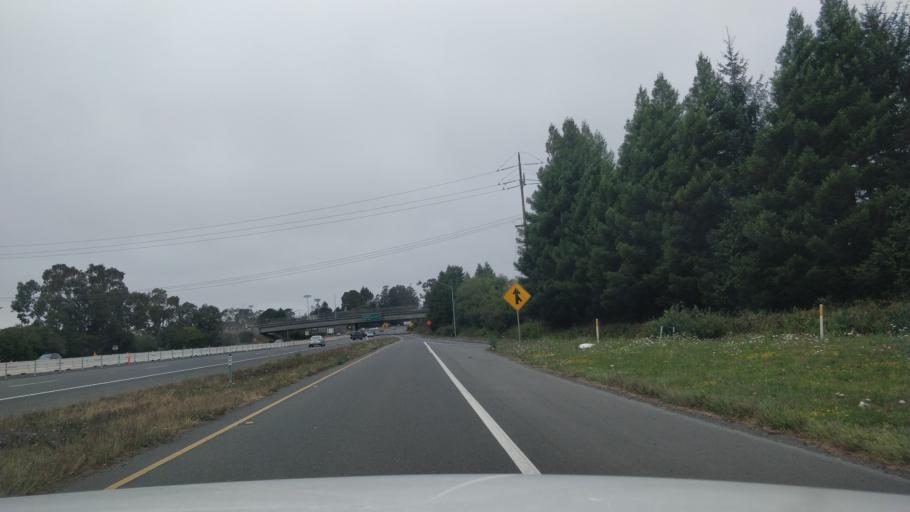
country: US
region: California
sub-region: Humboldt County
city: Arcata
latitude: 40.8638
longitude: -124.0826
